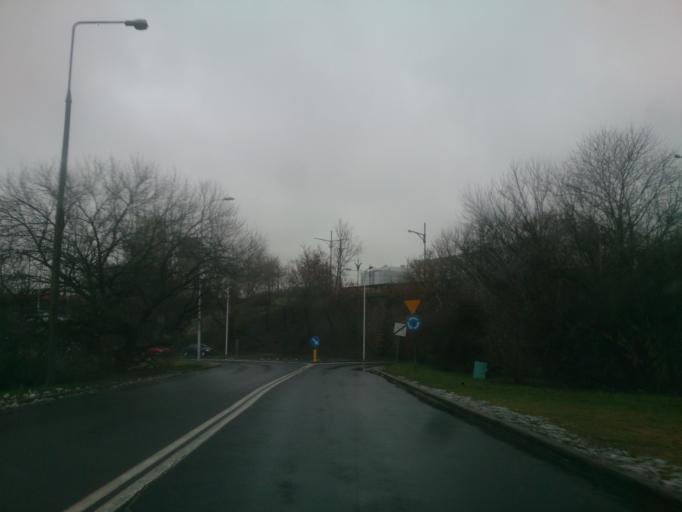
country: PL
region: Masovian Voivodeship
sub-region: Warszawa
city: Praga Polnoc
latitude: 52.2363
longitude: 21.0364
